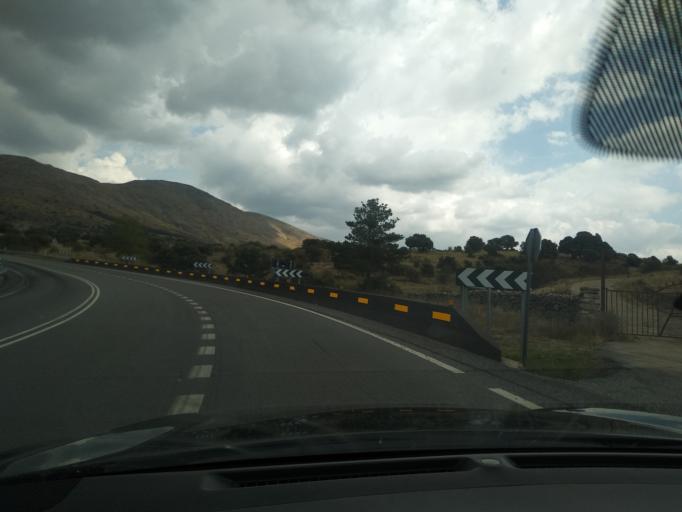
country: ES
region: Castille and Leon
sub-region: Provincia de Segovia
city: Otero de Herreros
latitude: 40.7665
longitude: -4.2033
